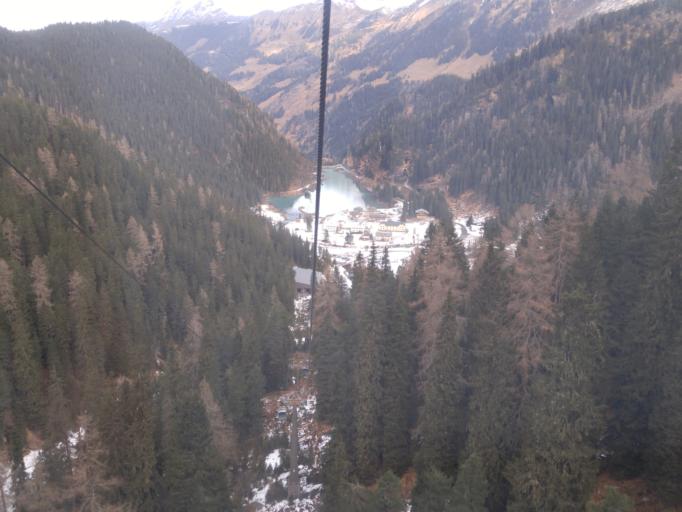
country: AT
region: Salzburg
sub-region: Politischer Bezirk Zell am See
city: Niedernsill
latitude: 47.1647
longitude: 12.6241
